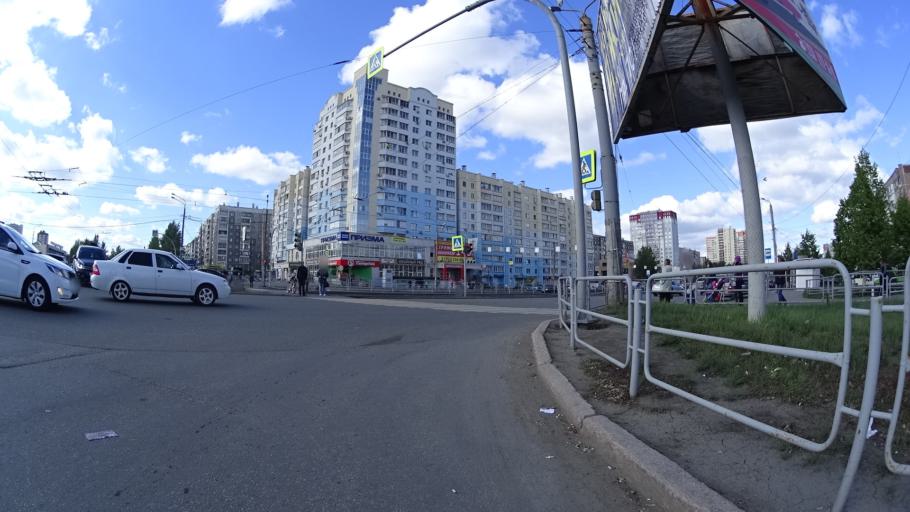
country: RU
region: Chelyabinsk
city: Roshchino
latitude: 55.1826
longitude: 61.2927
